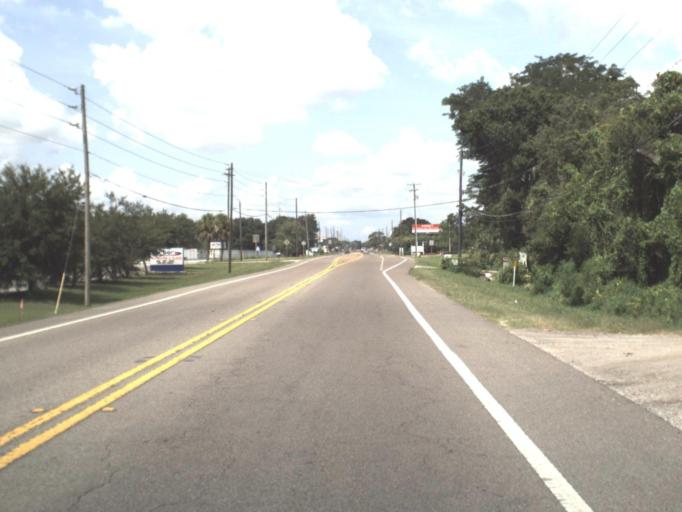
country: US
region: Florida
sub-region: Pasco County
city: Zephyrhills West
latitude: 28.2284
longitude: -82.2278
